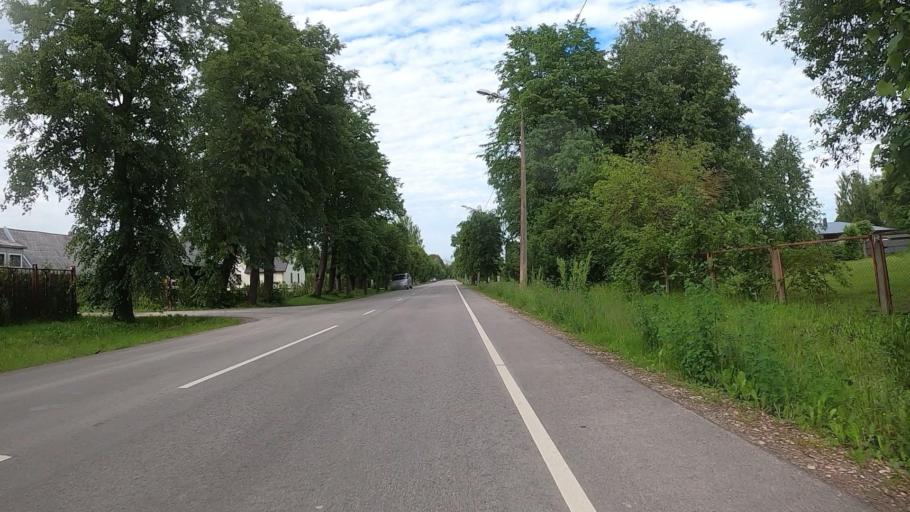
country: LV
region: Jelgava
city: Jelgava
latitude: 56.6651
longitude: 23.7469
